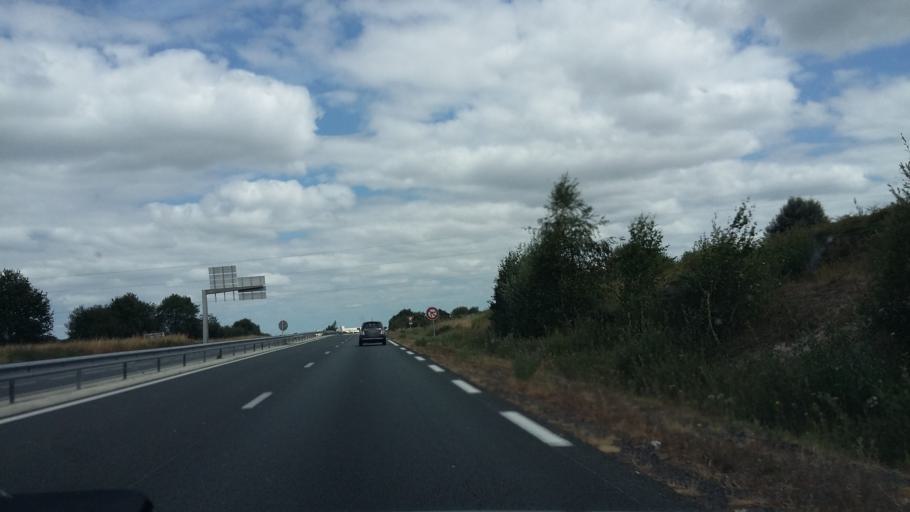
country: FR
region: Pays de la Loire
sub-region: Departement de la Vendee
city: La Chaize-le-Vicomte
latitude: 46.6632
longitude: -1.2663
